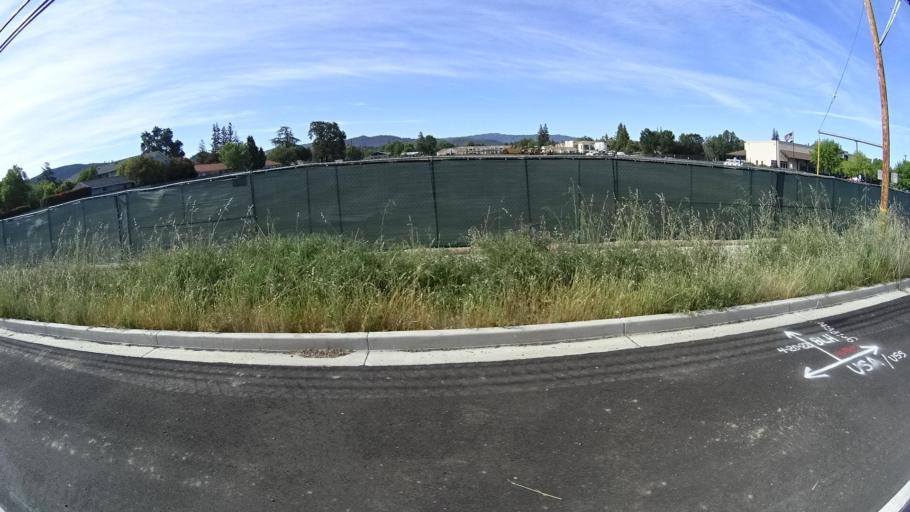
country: US
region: California
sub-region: Lake County
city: Kelseyville
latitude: 38.9821
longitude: -122.8345
